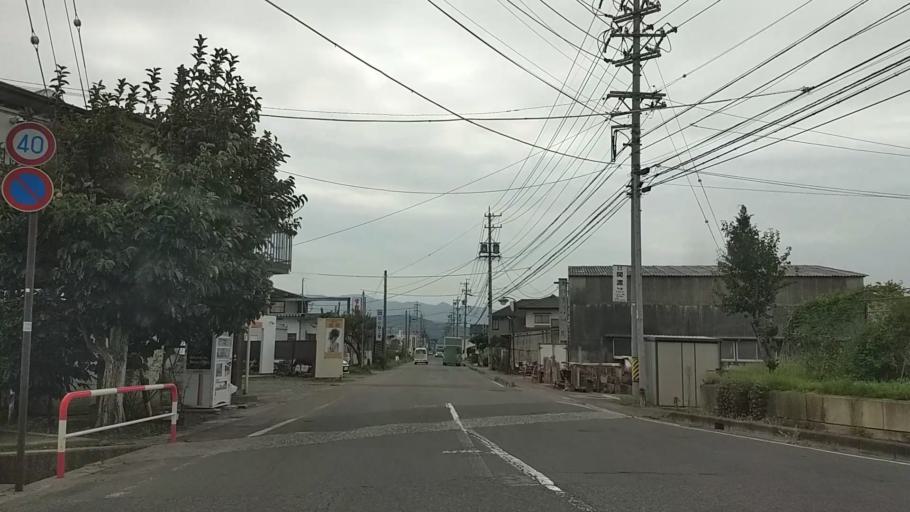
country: JP
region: Nagano
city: Nagano-shi
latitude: 36.6119
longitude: 138.2092
